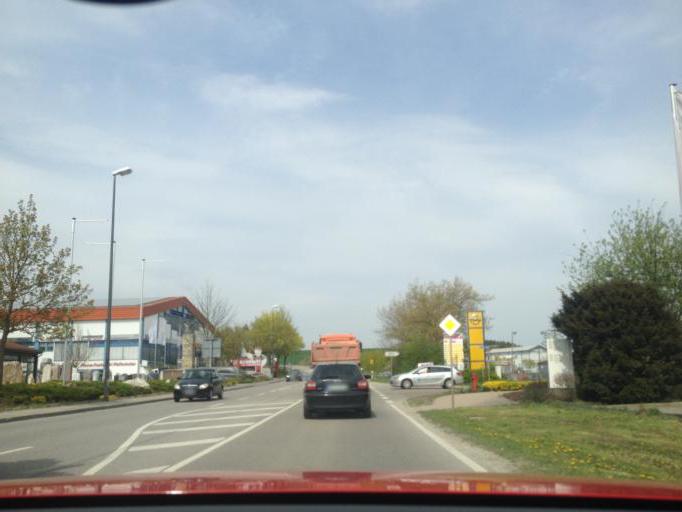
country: DE
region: Bavaria
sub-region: Upper Bavaria
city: Pfaffenhofen an der Ilm
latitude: 48.5447
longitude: 11.5116
